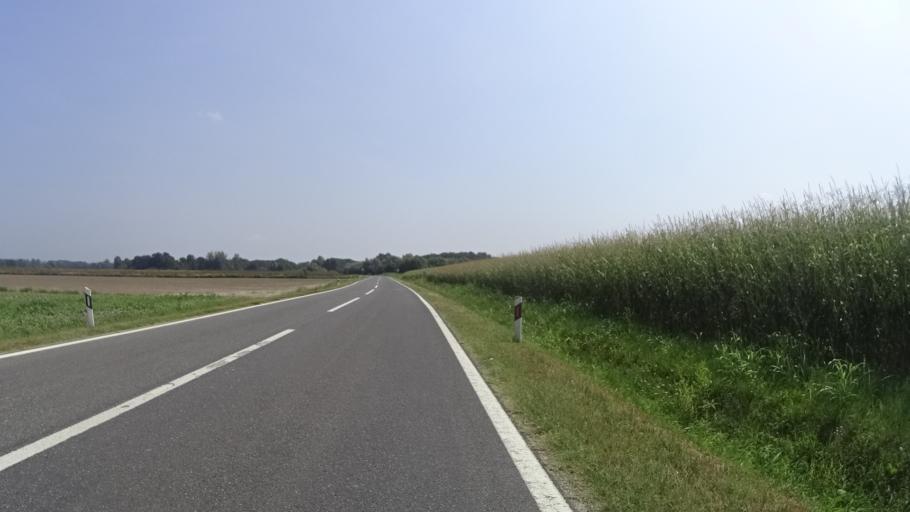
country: HR
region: Medimurska
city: Hodosan
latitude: 46.3994
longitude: 16.6521
